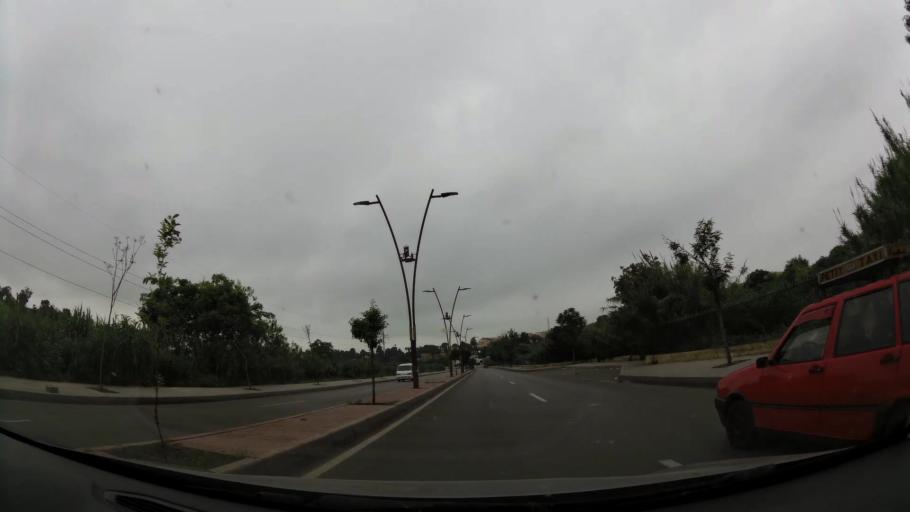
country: MA
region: Fes-Boulemane
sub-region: Fes
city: Fes
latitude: 34.0514
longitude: -4.9859
